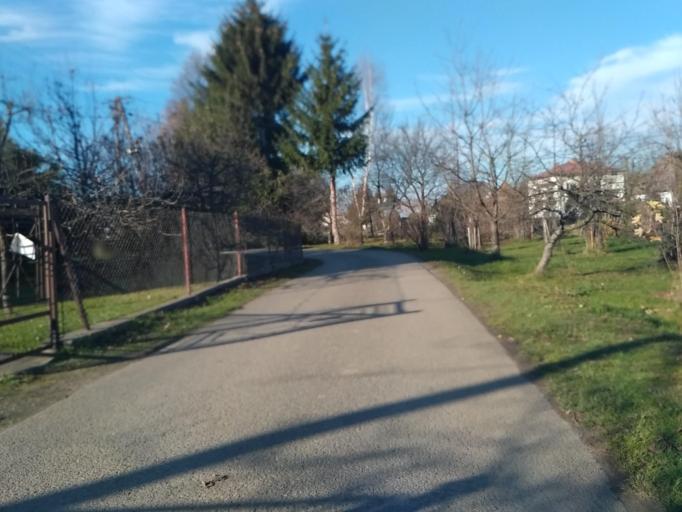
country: PL
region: Subcarpathian Voivodeship
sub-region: Powiat brzozowski
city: Humniska
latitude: 49.6747
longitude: 22.0482
